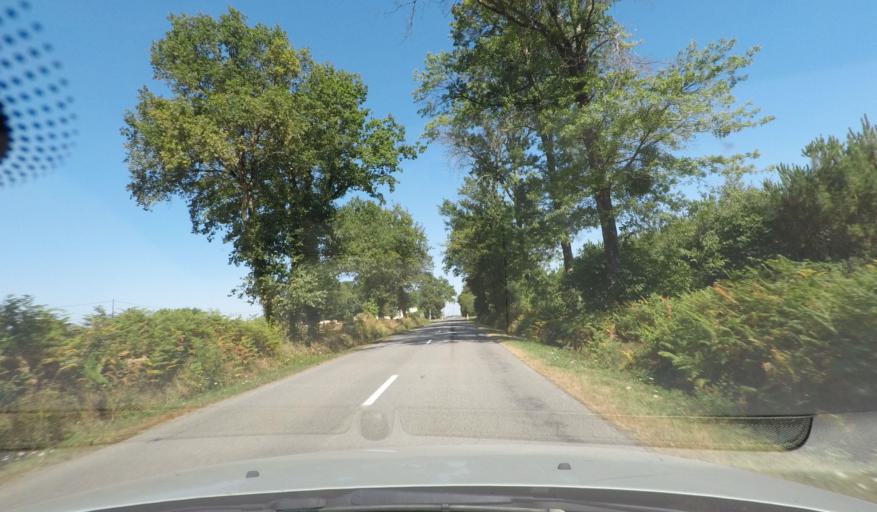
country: FR
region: Brittany
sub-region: Departement du Morbihan
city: Ruffiac
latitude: 47.8463
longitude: -2.2776
